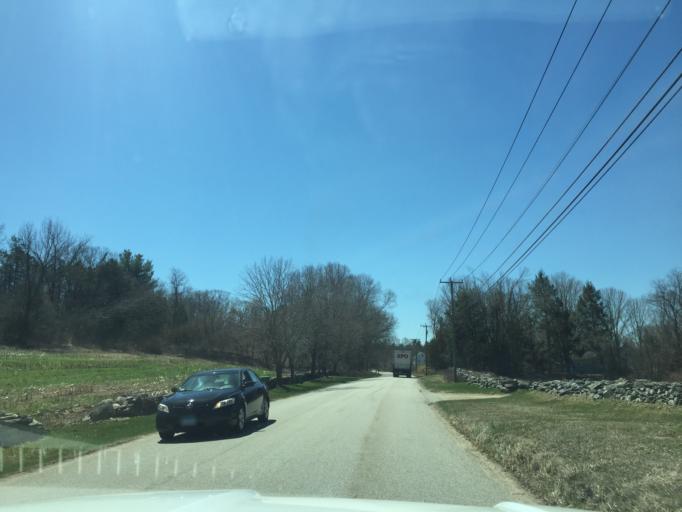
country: US
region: Connecticut
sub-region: Windham County
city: Quinebaug
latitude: 41.9871
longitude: -71.9521
